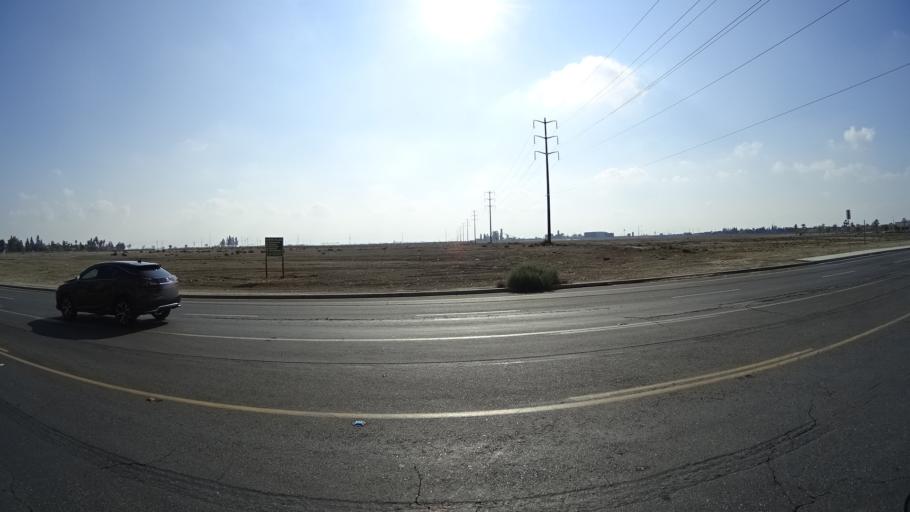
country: US
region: California
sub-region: Kern County
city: Greenacres
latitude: 35.3035
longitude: -119.0957
